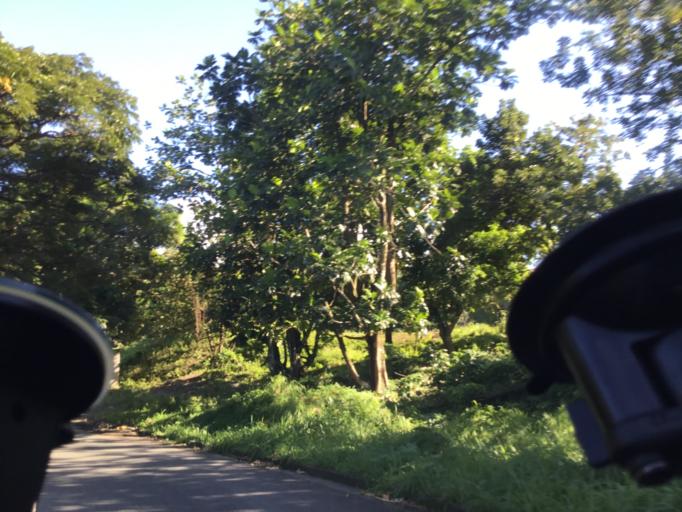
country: VC
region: Saint David
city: Chateaubelair
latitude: 13.3014
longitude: -61.2291
